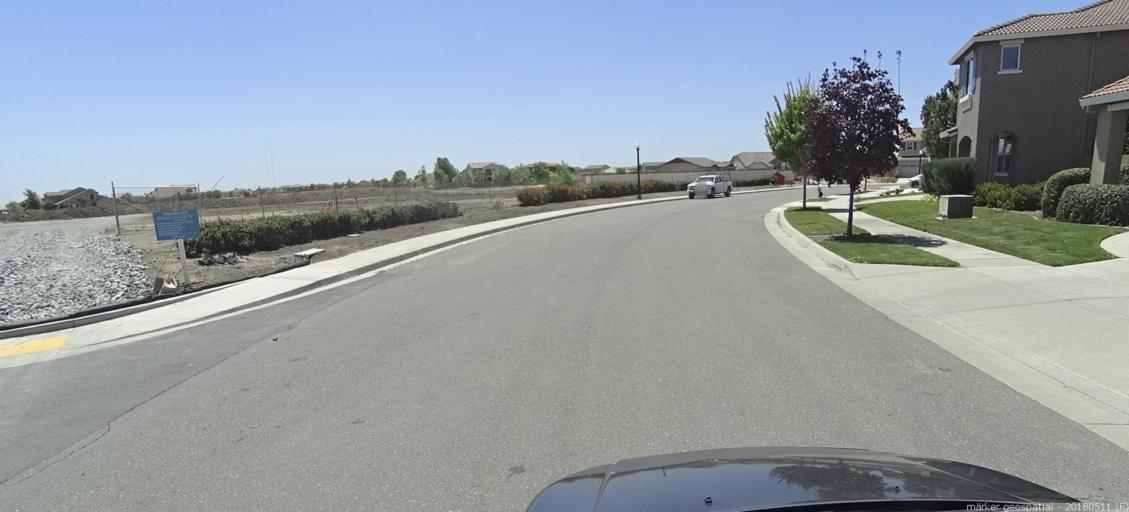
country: US
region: California
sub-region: Yolo County
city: West Sacramento
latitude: 38.6500
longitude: -121.5465
